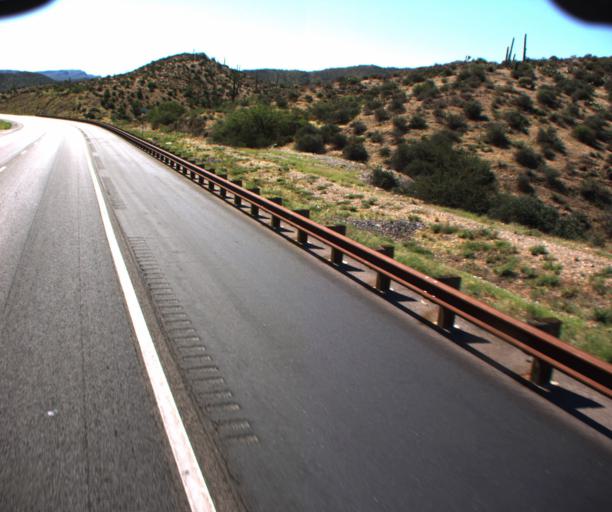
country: US
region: Arizona
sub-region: Pinal County
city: Gold Camp
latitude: 33.2753
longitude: -111.2275
